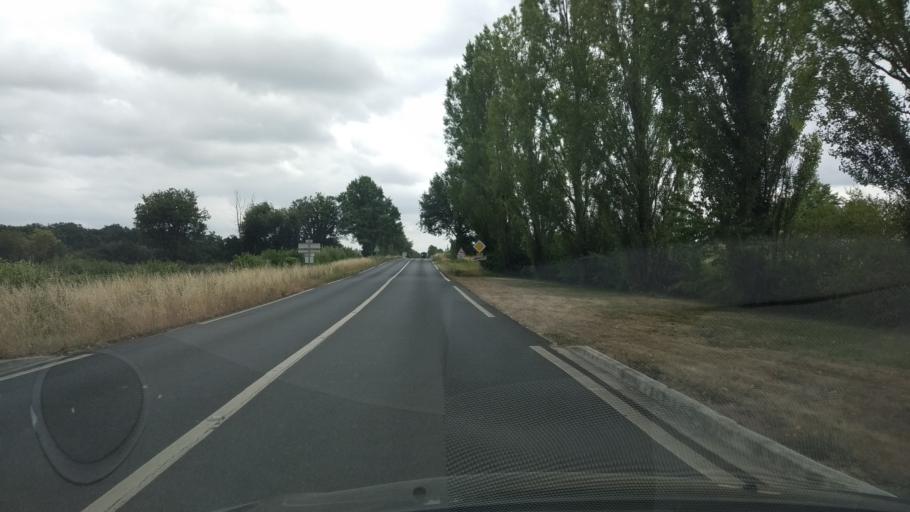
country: FR
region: Poitou-Charentes
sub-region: Departement de la Vienne
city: Smarves
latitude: 46.5048
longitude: 0.3619
